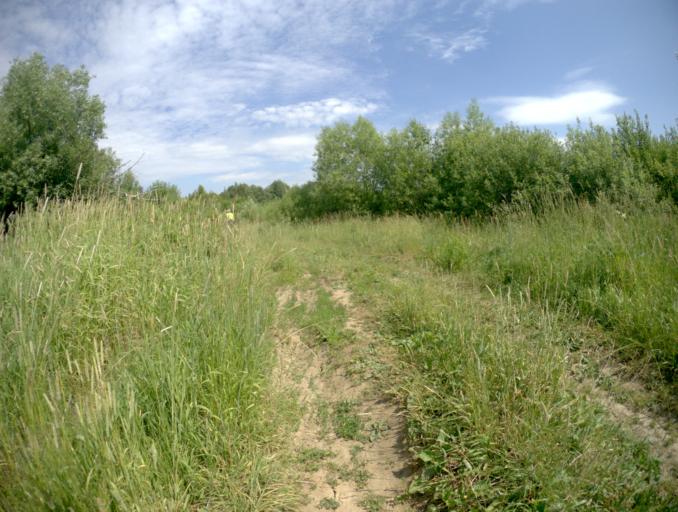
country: RU
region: Vladimir
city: Vorsha
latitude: 56.0265
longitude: 40.1828
